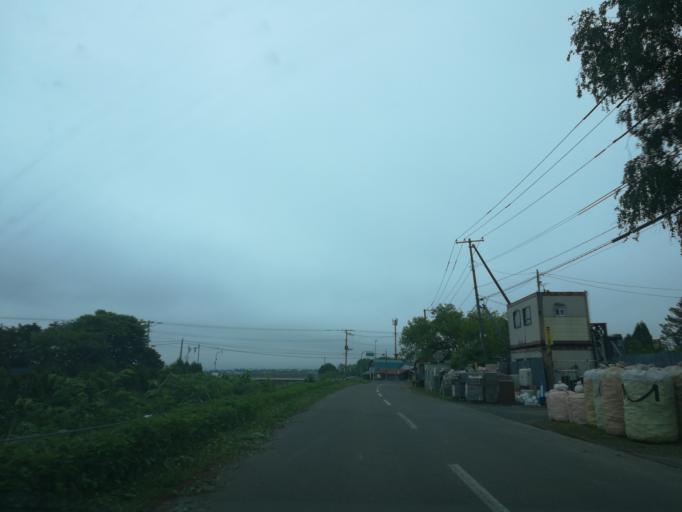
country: JP
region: Hokkaido
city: Ebetsu
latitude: 43.0718
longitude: 141.6459
